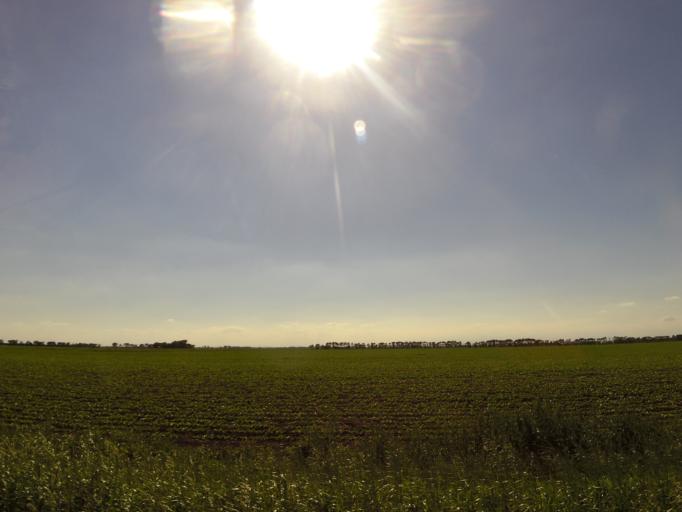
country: US
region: North Dakota
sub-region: Walsh County
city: Grafton
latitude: 48.3403
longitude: -97.2330
